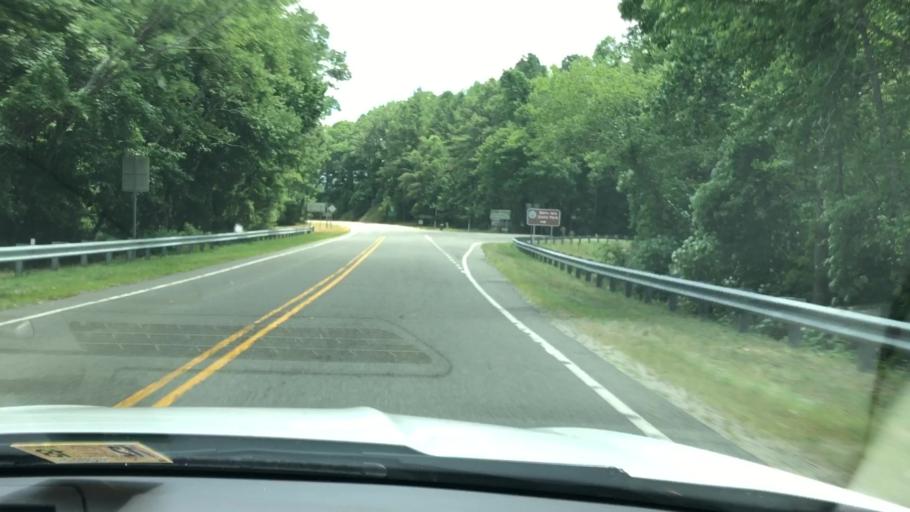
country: US
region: Virginia
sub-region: Lancaster County
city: Lancaster
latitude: 37.8300
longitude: -76.5766
